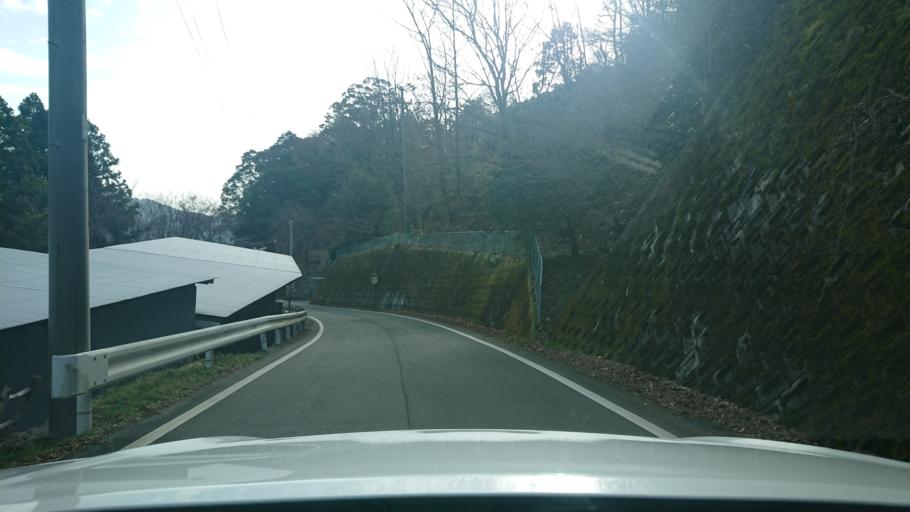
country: JP
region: Tokushima
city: Ishii
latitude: 33.9147
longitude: 134.4070
